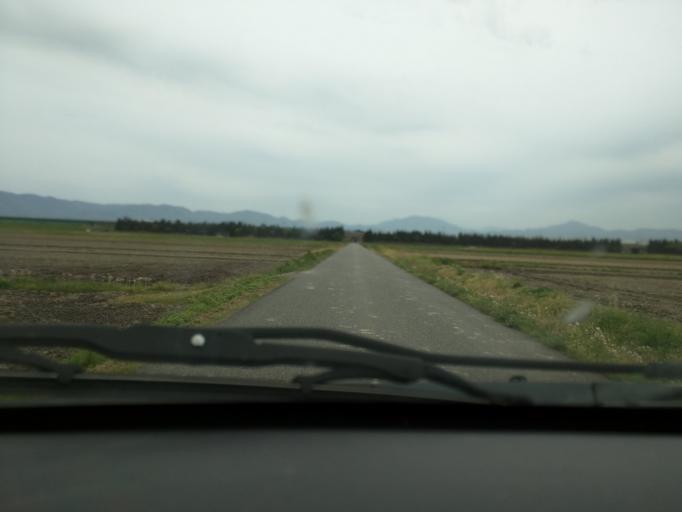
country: JP
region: Fukushima
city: Kitakata
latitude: 37.5344
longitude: 139.8652
